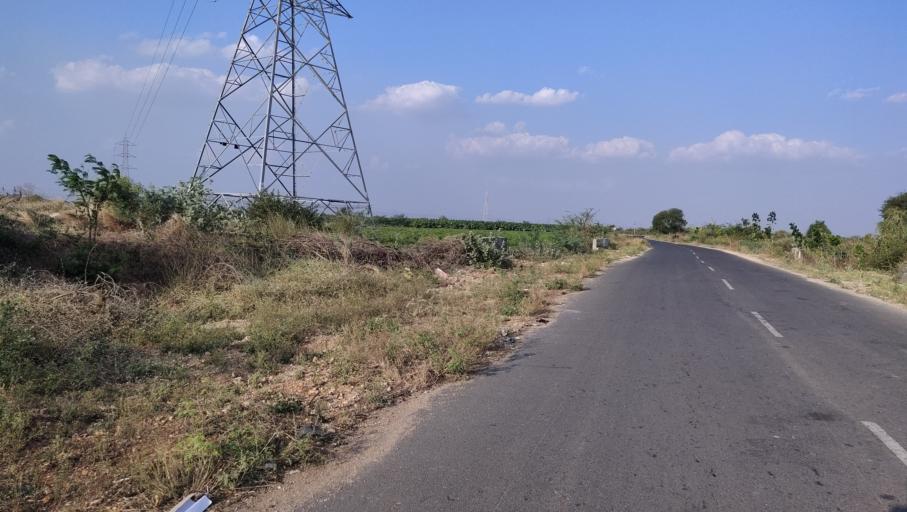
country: IN
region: Andhra Pradesh
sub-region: Anantapur
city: Tadpatri
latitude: 14.9493
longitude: 77.8797
